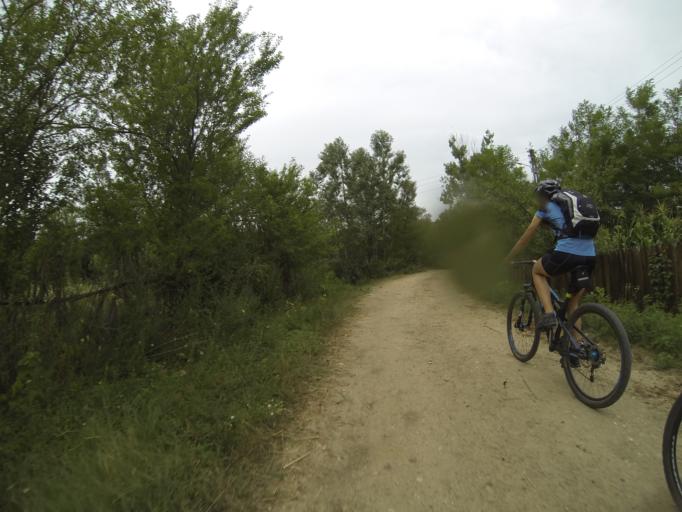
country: RO
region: Dolj
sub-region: Comuna Bradesti
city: Bradesti
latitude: 44.5299
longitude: 23.6257
